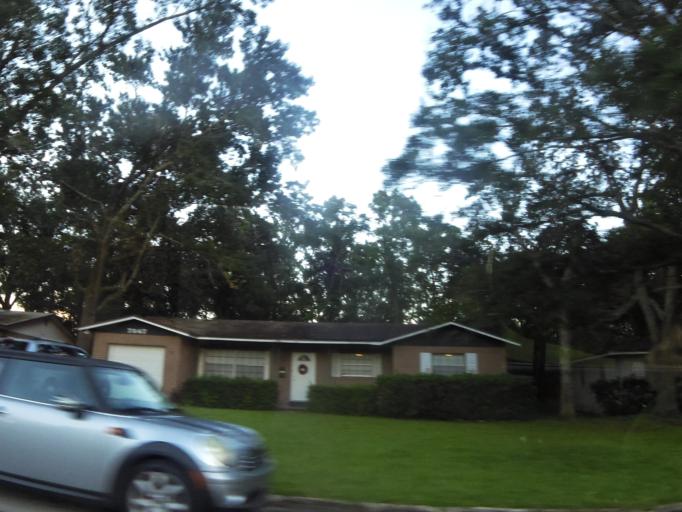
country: US
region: Florida
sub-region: Duval County
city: Jacksonville
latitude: 30.2380
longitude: -81.6037
